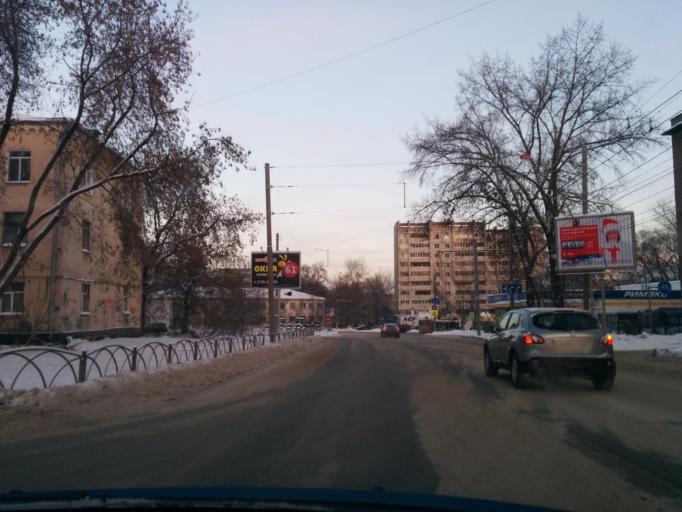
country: RU
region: Perm
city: Perm
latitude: 57.9988
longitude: 56.2718
